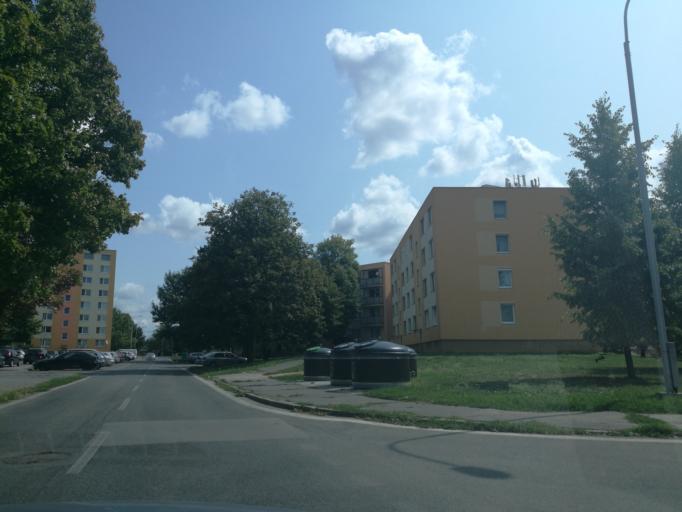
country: SK
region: Nitriansky
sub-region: Okres Nitra
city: Nitra
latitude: 48.3063
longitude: 18.1133
